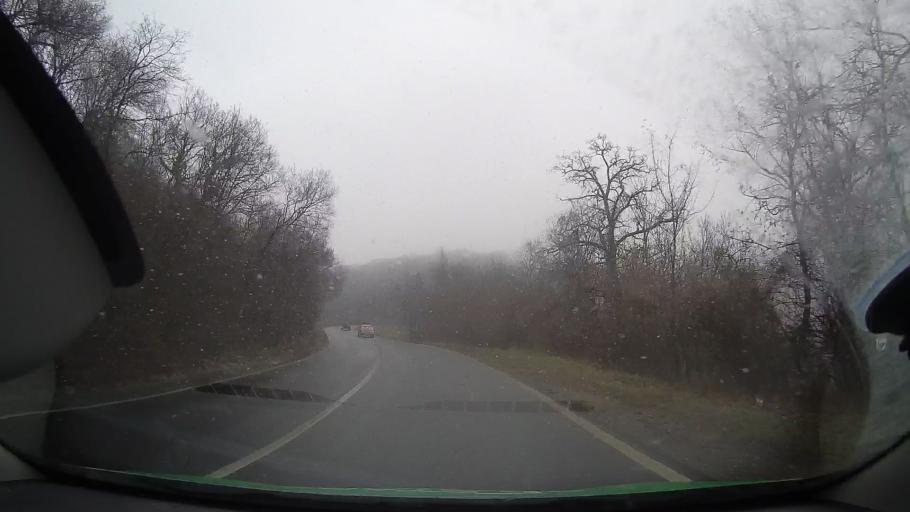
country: RO
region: Sibiu
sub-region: Municipiul Medias
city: Medias
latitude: 46.1797
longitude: 24.3395
